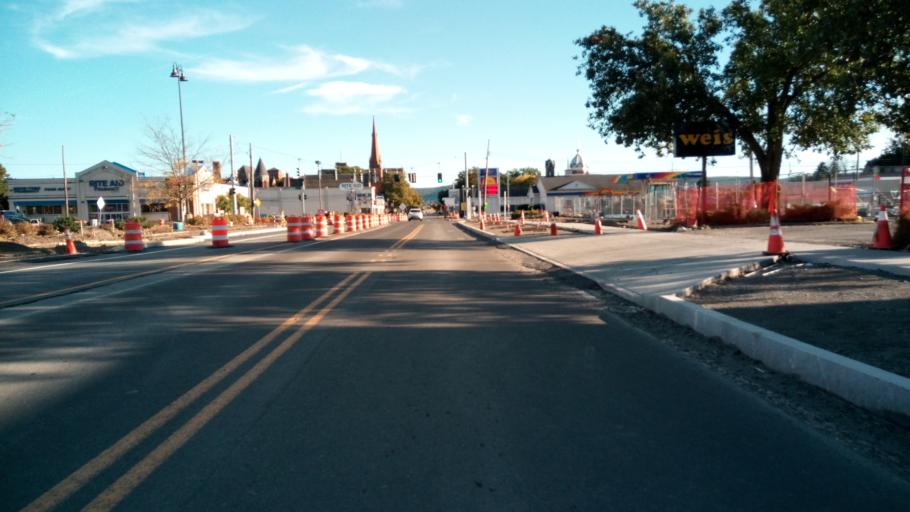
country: US
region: New York
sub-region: Chemung County
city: Elmira
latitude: 42.0921
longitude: -76.8095
